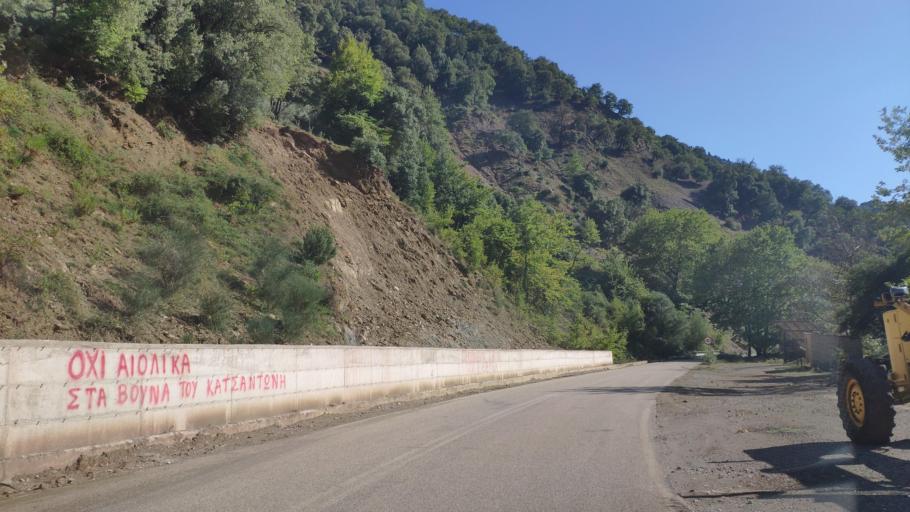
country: GR
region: Central Greece
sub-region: Nomos Evrytanias
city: Kerasochori
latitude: 39.0576
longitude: 21.6070
